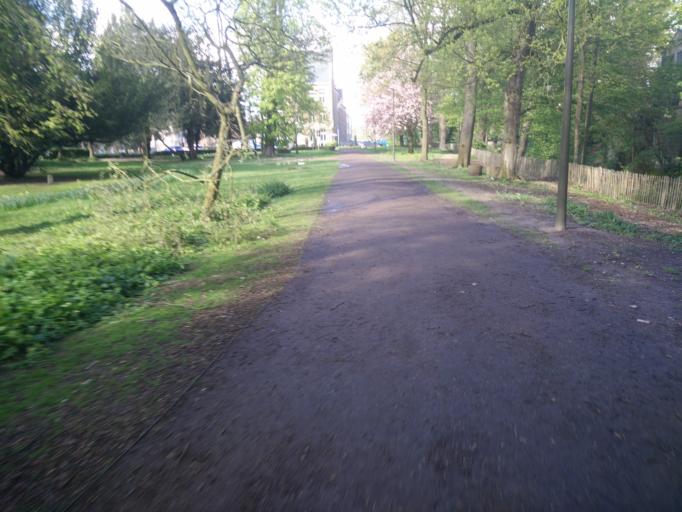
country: BE
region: Flanders
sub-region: Provincie Vlaams-Brabant
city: Halle
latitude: 50.7338
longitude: 4.2386
